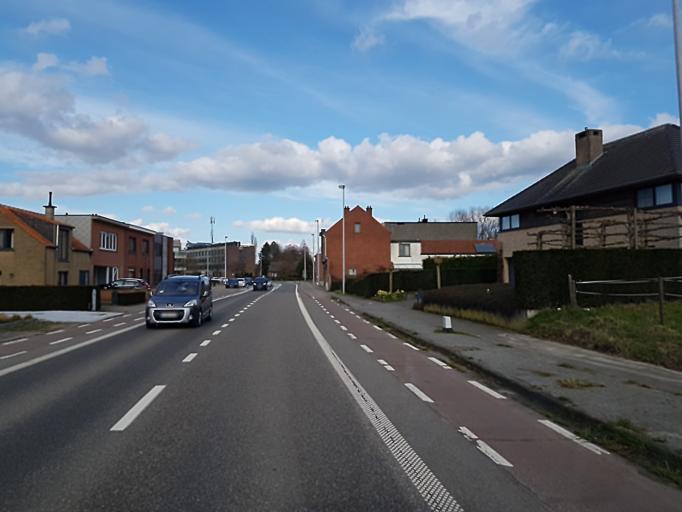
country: BE
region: Flanders
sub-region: Provincie Oost-Vlaanderen
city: Sint-Niklaas
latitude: 51.1910
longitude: 4.1708
